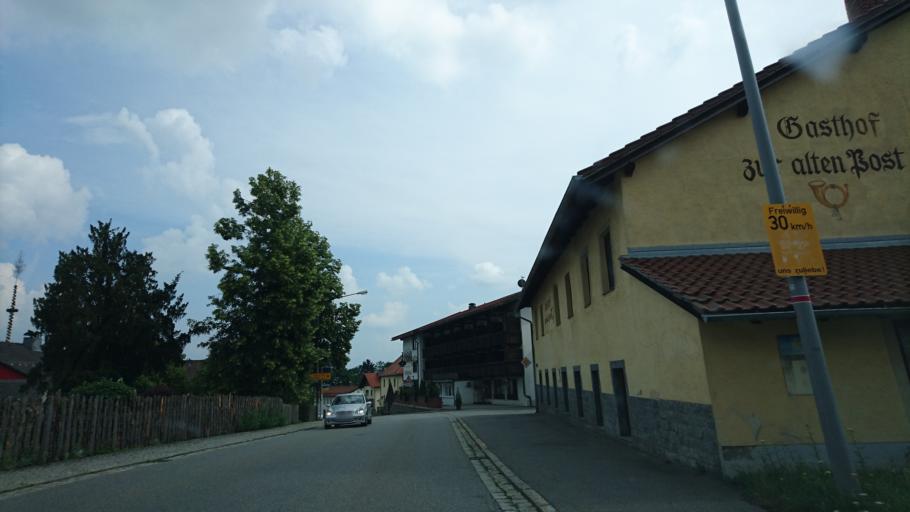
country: DE
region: Bavaria
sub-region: Lower Bavaria
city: Eppenschlag
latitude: 48.9227
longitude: 13.3189
